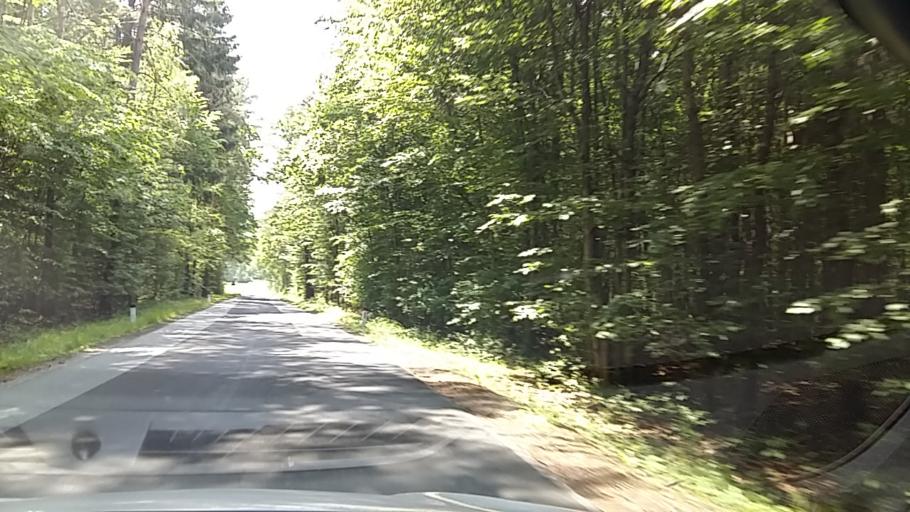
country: AT
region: Styria
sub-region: Politischer Bezirk Hartberg-Fuerstenfeld
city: Bad Blumau
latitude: 47.1237
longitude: 16.0263
